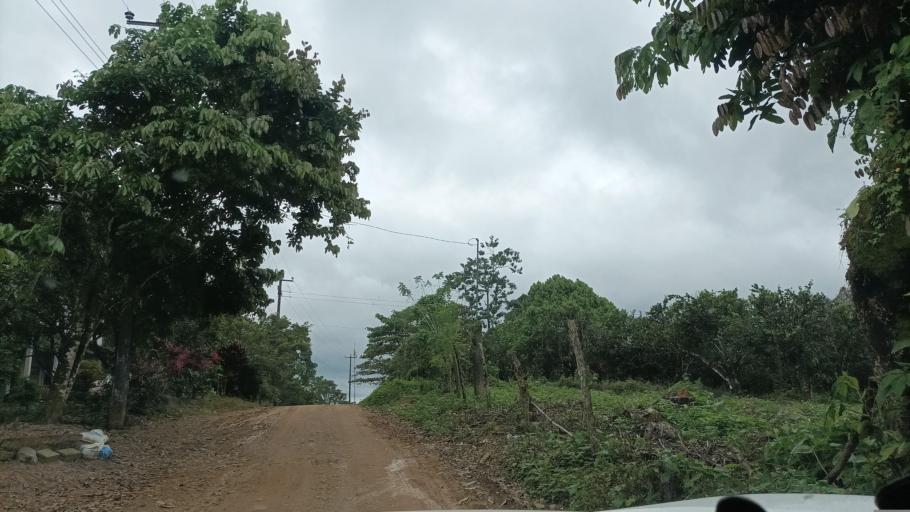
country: MX
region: Veracruz
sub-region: Uxpanapa
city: Poblado 10
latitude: 17.2712
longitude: -94.4985
